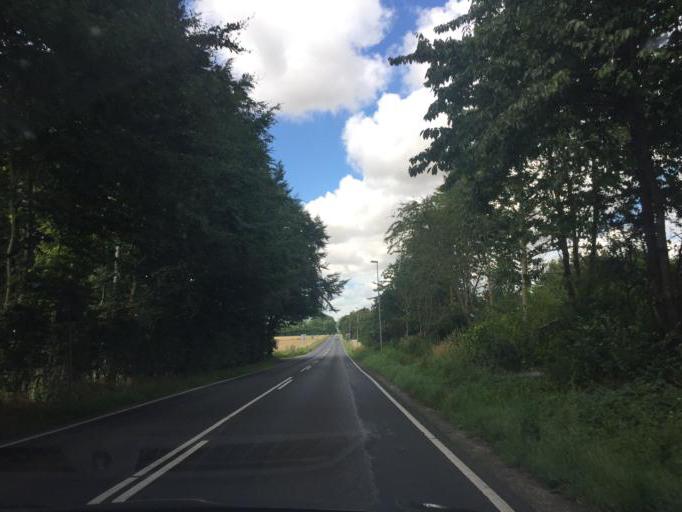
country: DK
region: South Denmark
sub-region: Odense Kommune
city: Stige
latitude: 55.4540
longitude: 10.3687
